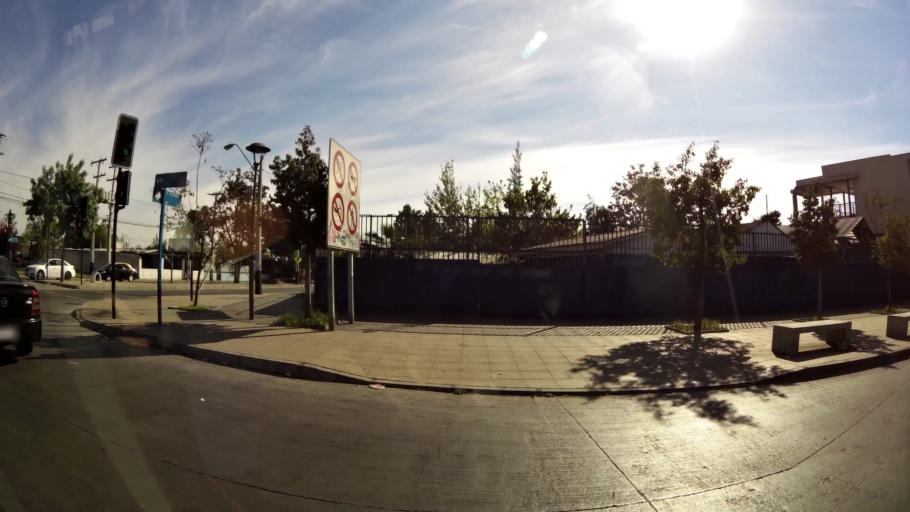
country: CL
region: Santiago Metropolitan
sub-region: Provincia de Santiago
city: La Pintana
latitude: -33.5377
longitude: -70.6208
